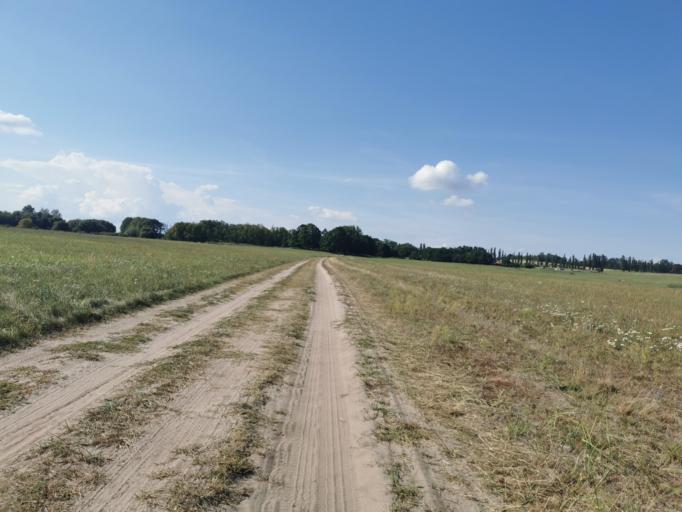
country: SK
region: Trnavsky
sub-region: Okres Senica
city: Senica
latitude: 48.5965
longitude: 17.2513
